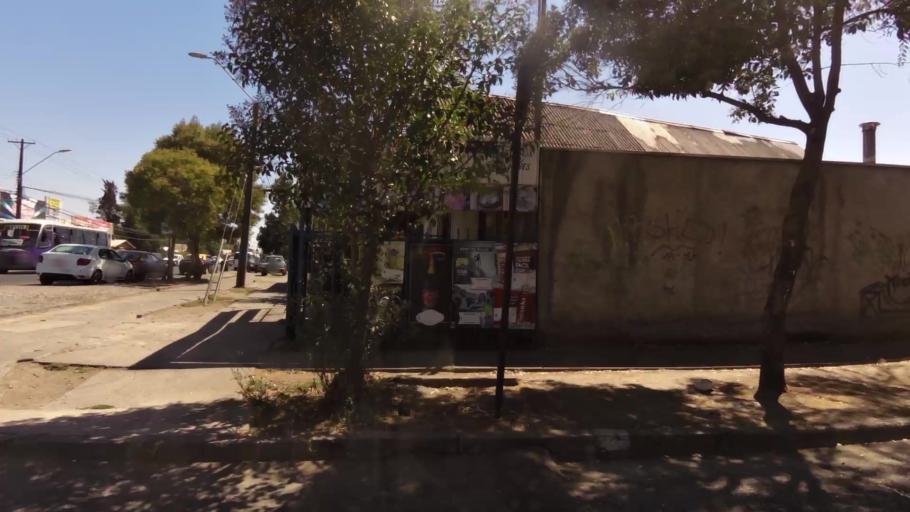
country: CL
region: Maule
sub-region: Provincia de Curico
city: Curico
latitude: -34.9711
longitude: -71.2479
